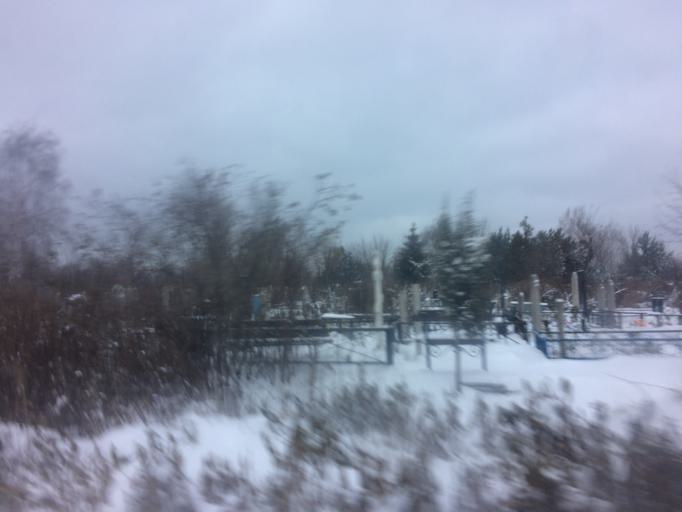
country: RU
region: Tula
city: Mendeleyevskiy
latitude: 54.1433
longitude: 37.6464
